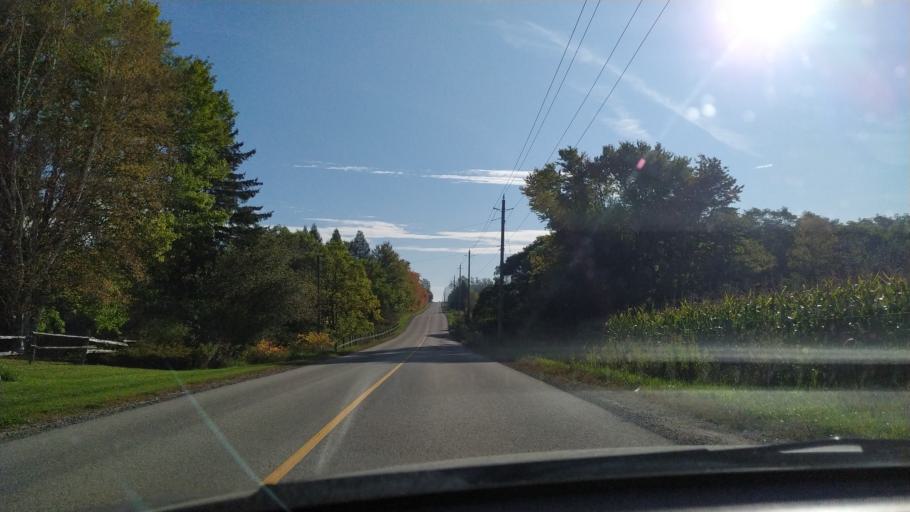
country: CA
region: Ontario
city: Stratford
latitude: 43.4957
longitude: -80.7596
